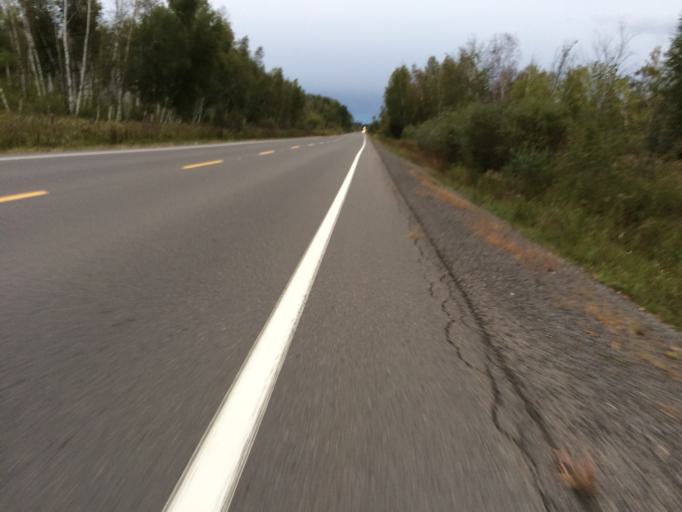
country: CA
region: Ontario
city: Ottawa
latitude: 45.3041
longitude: -75.6421
